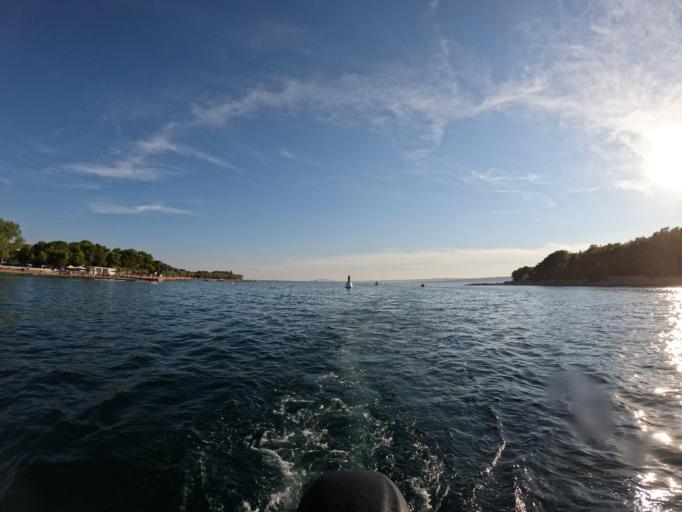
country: HR
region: Primorsko-Goranska
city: Punat
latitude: 45.0153
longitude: 14.6238
